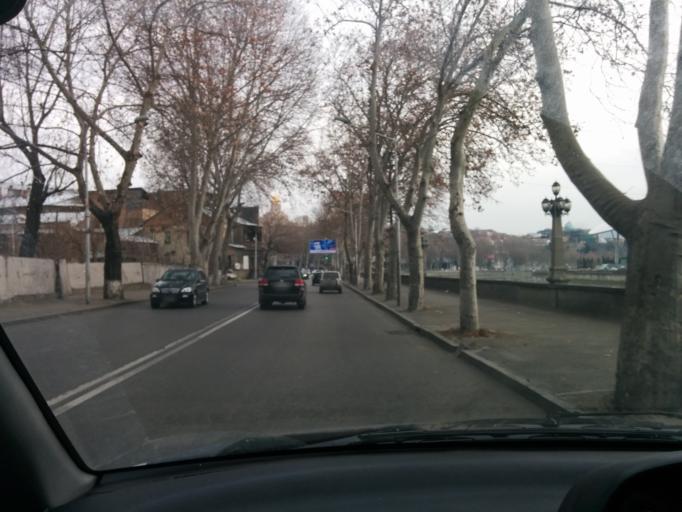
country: GE
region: T'bilisi
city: Tbilisi
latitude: 41.7023
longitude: 44.8049
